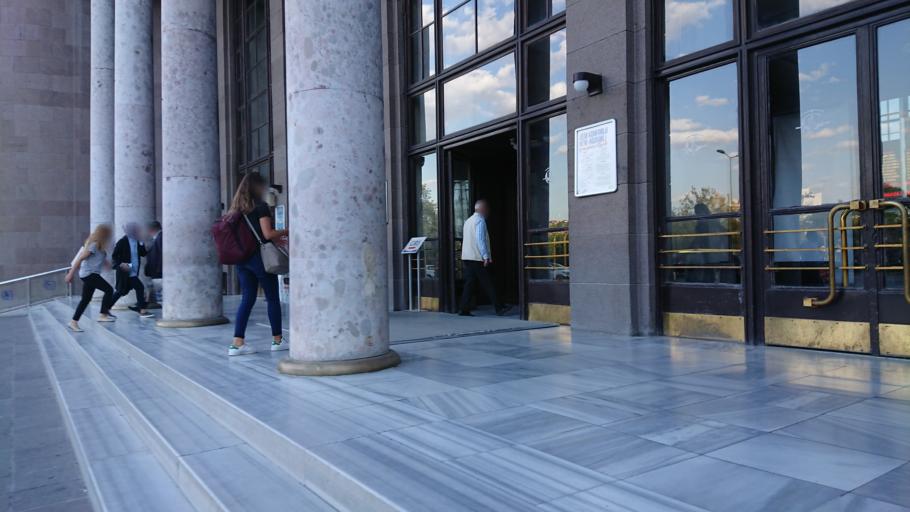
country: TR
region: Ankara
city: Ankara
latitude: 39.9363
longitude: 32.8437
